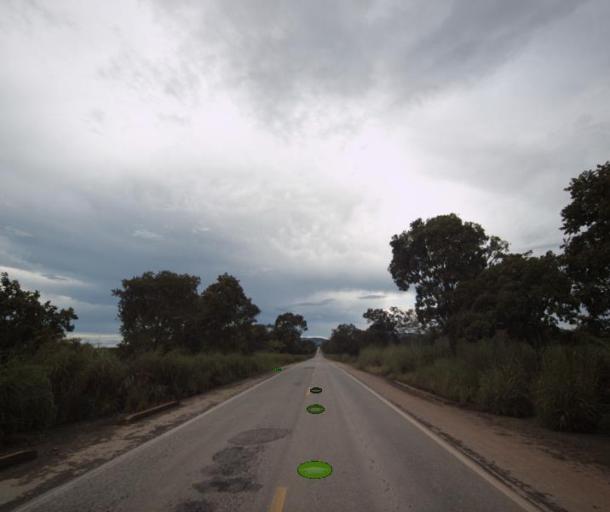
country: BR
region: Goias
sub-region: Porangatu
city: Porangatu
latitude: -13.5609
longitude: -49.0584
